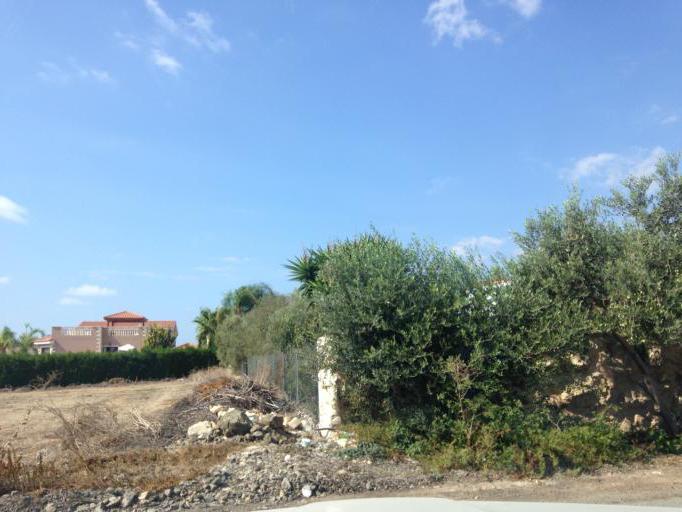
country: CY
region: Pafos
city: Pegeia
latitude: 34.8654
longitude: 32.3568
